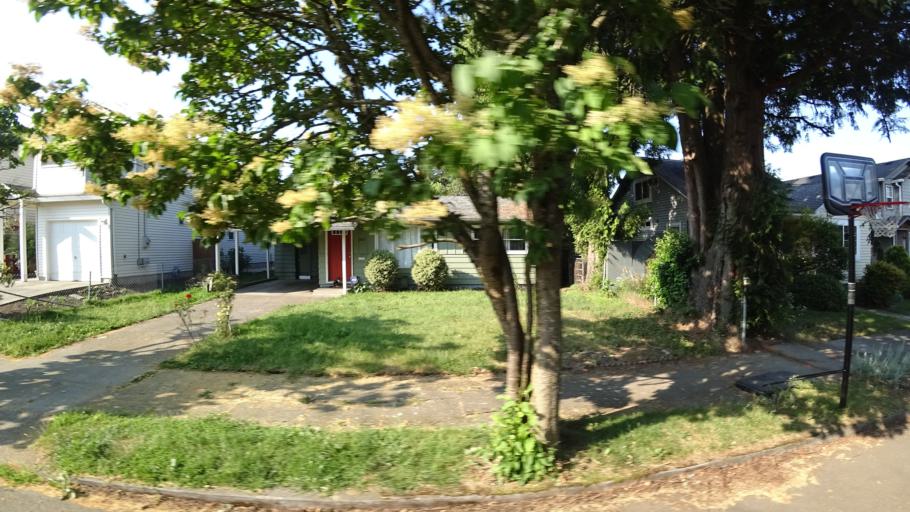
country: US
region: Oregon
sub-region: Washington County
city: West Haven
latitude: 45.5910
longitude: -122.7344
